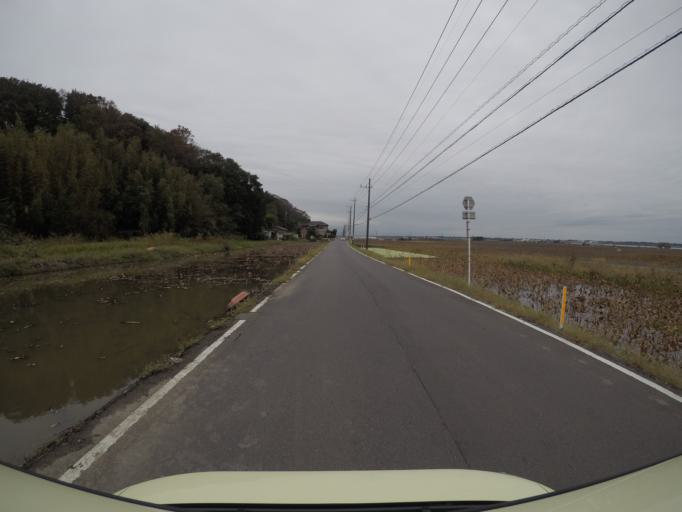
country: JP
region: Ibaraki
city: Ami
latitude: 36.0846
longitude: 140.2431
